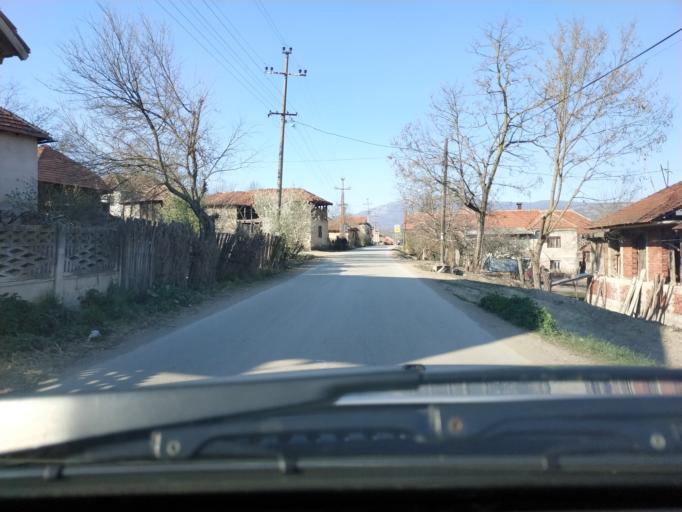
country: RS
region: Central Serbia
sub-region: Nisavski Okrug
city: Aleksinac
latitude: 43.5087
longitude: 21.7971
